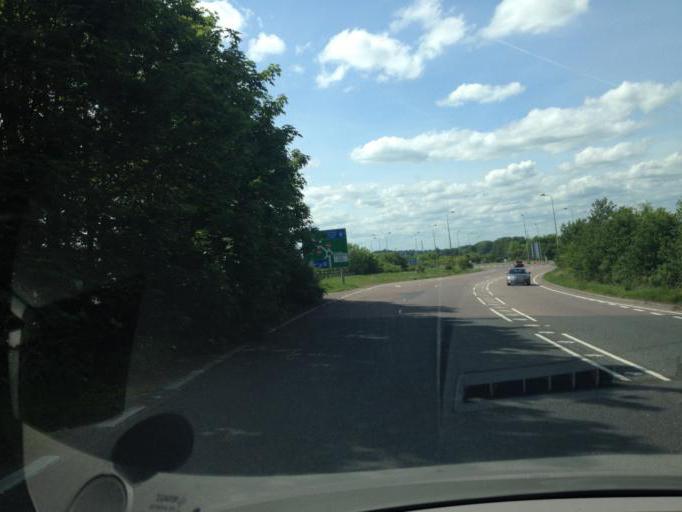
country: GB
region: England
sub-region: Oxfordshire
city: Wheatley
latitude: 51.7391
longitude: -1.0922
